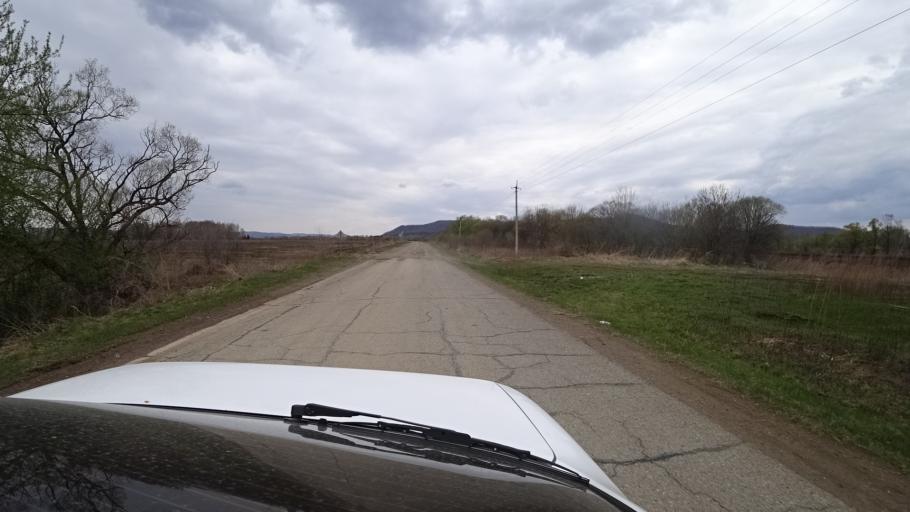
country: RU
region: Primorskiy
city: Novopokrovka
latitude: 45.5534
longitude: 134.3602
